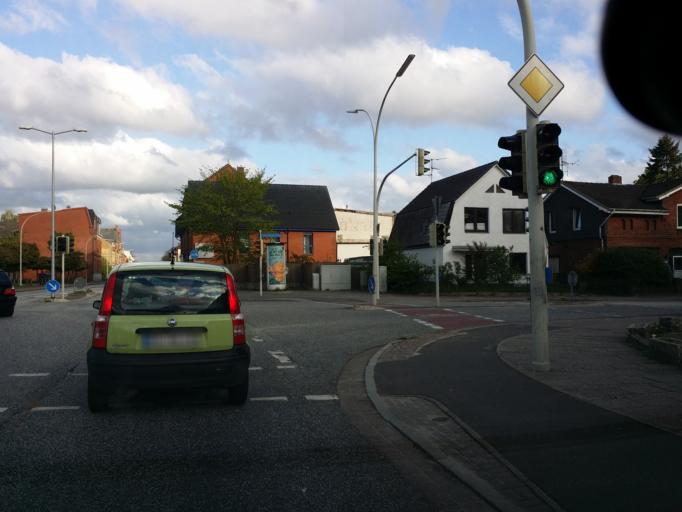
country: DE
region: Schleswig-Holstein
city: Rendsburg
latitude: 54.3111
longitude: 9.6544
